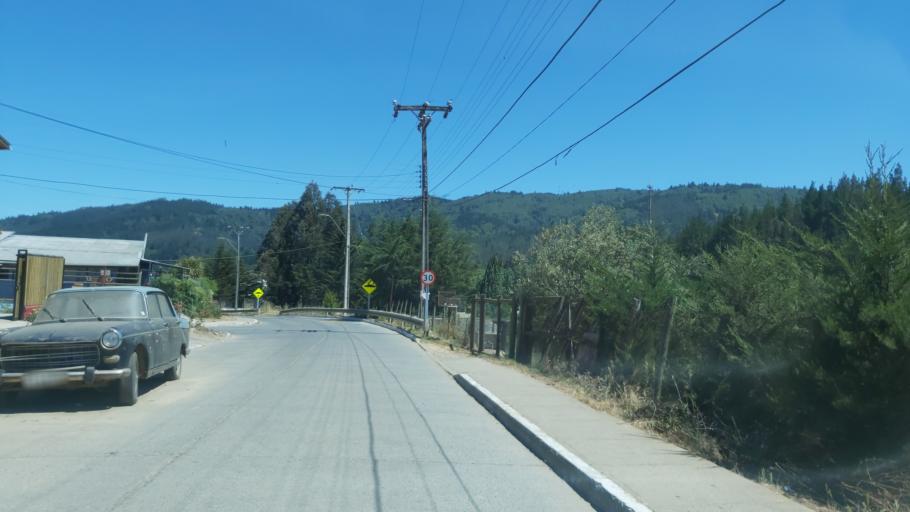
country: CL
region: Maule
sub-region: Provincia de Talca
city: Talca
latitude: -34.9836
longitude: -71.9804
